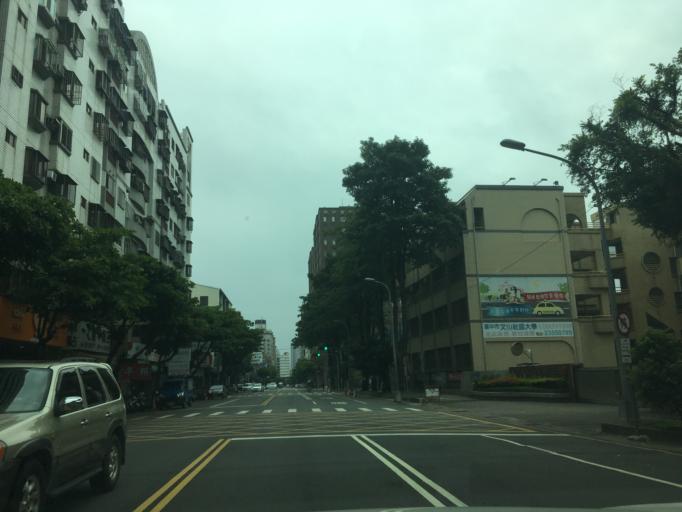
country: TW
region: Taiwan
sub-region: Taichung City
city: Taichung
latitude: 24.1688
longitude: 120.6602
